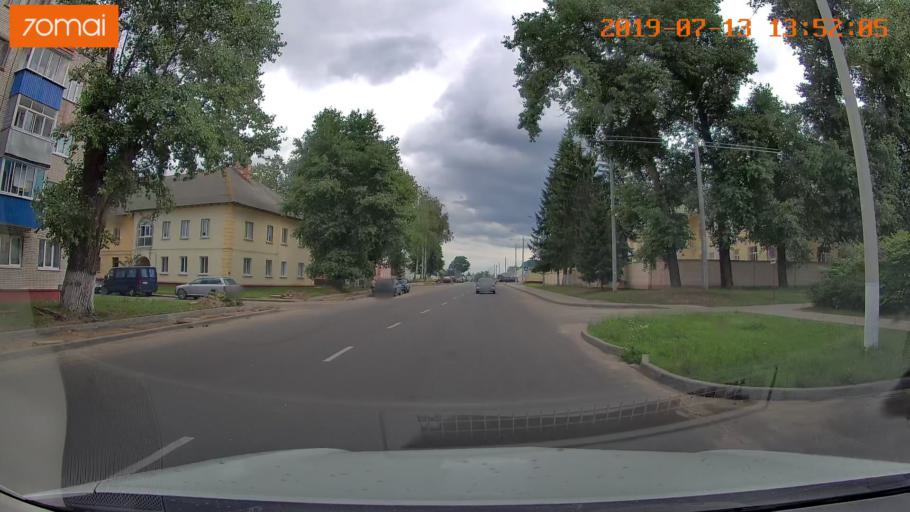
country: BY
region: Mogilev
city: Asipovichy
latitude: 53.2949
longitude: 28.6376
